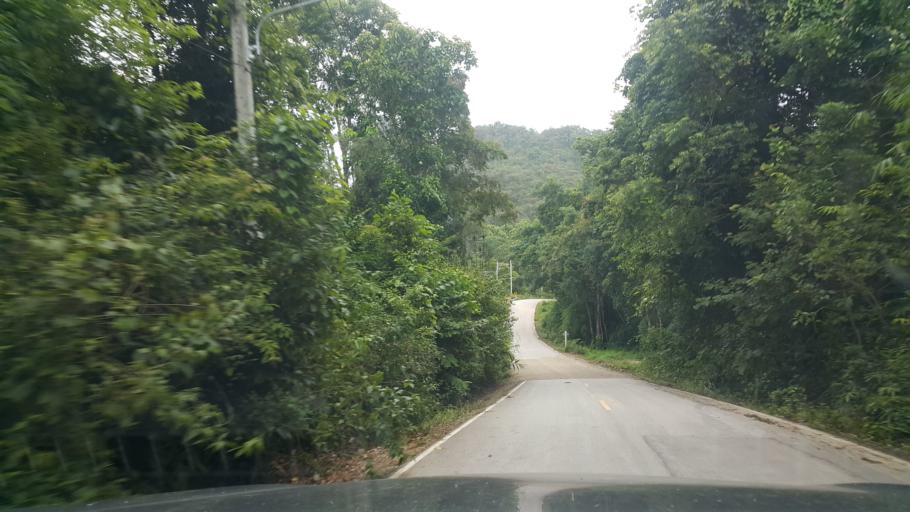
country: TH
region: Chiang Mai
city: San Sai
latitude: 18.9709
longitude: 99.1250
